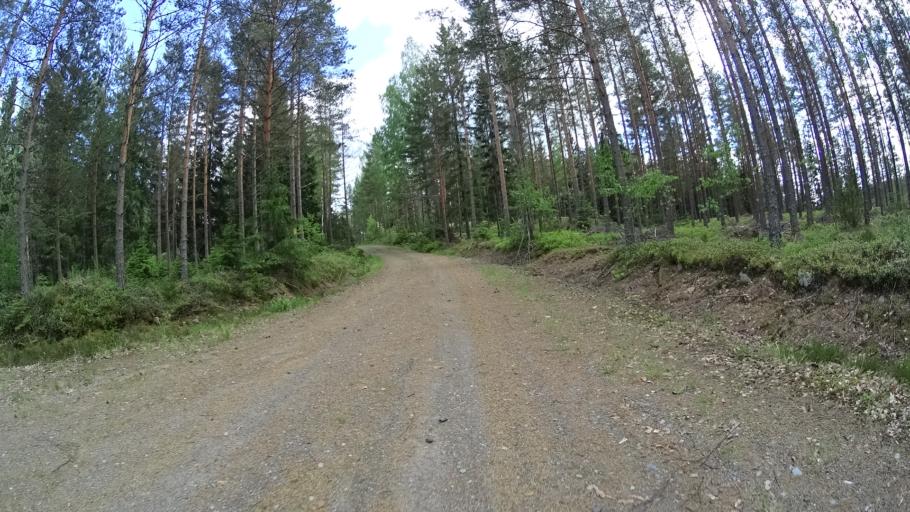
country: FI
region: Varsinais-Suomi
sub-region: Salo
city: Kisko
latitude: 60.1869
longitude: 23.5500
